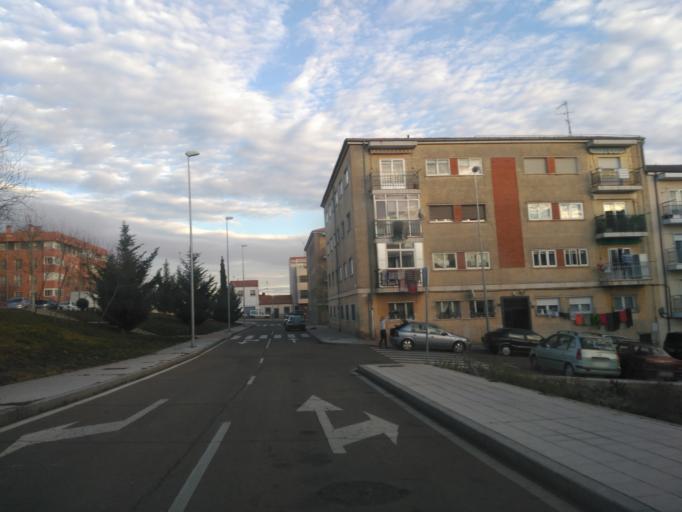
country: ES
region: Castille and Leon
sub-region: Provincia de Salamanca
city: Salamanca
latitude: 40.9791
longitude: -5.6727
